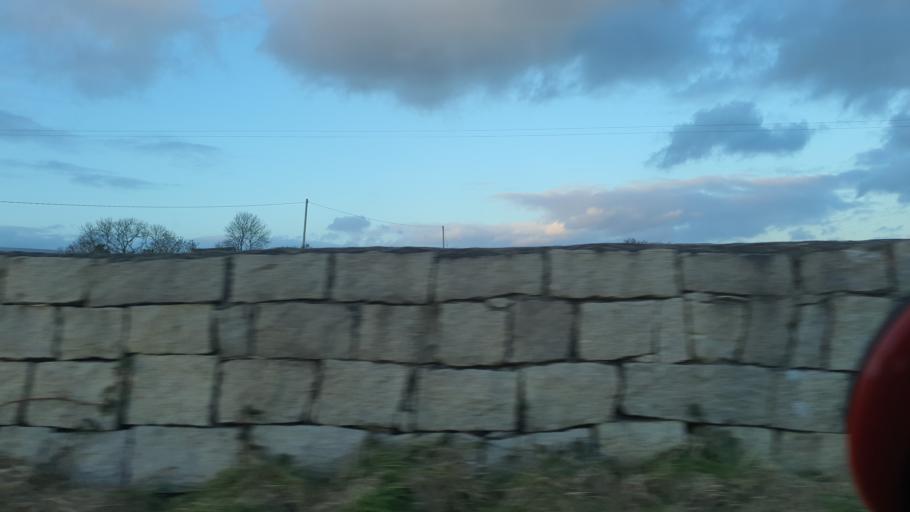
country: GB
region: Northern Ireland
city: Kilkeel
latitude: 54.0466
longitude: -6.0702
